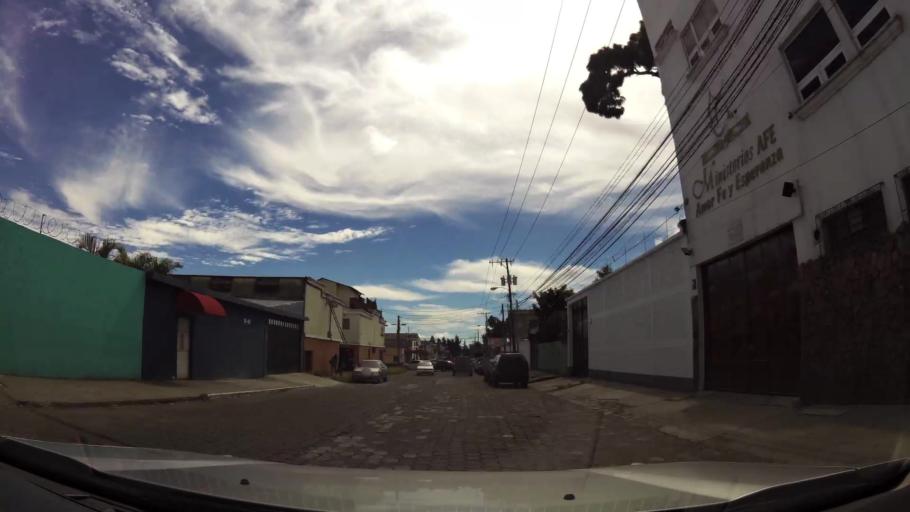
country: GT
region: Guatemala
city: Mixco
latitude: 14.6366
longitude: -90.5781
